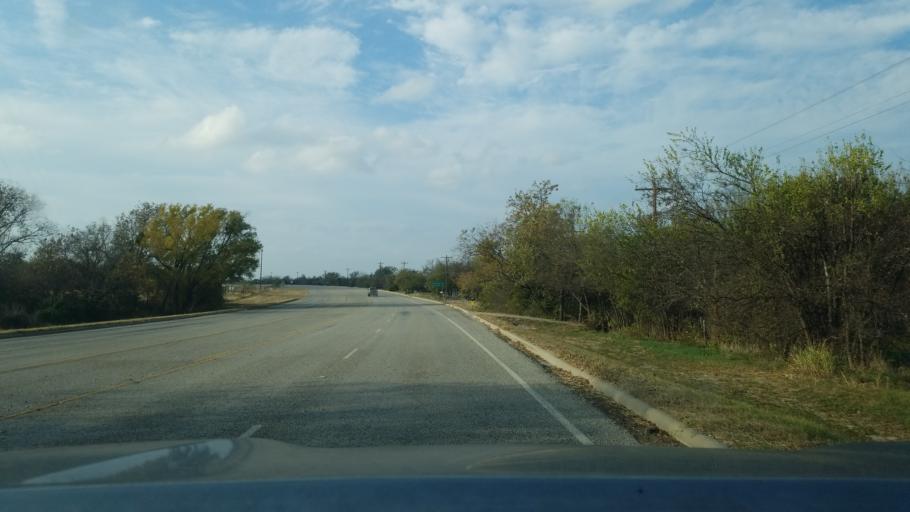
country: US
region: Texas
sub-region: Lampasas County
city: Lampasas
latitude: 31.2195
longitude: -98.3955
